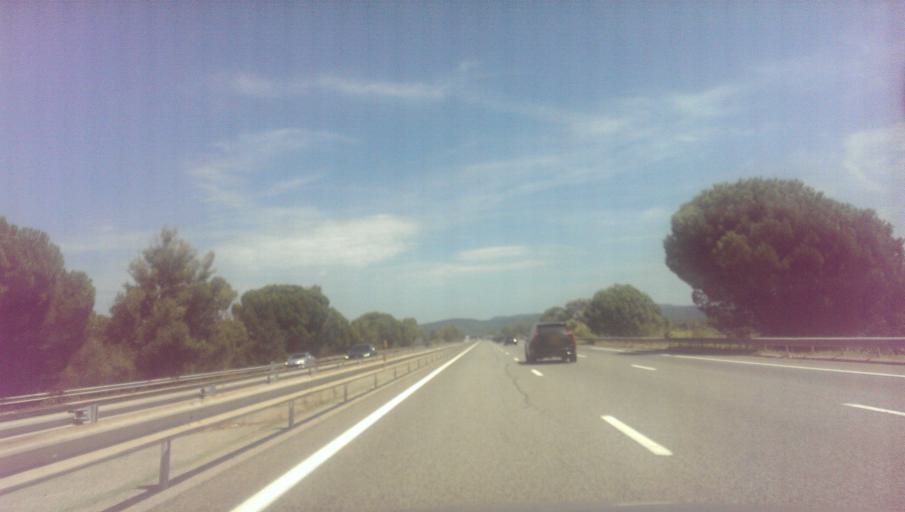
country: FR
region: Provence-Alpes-Cote d'Azur
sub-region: Departement du Var
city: Vidauban
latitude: 43.4025
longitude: 6.3942
